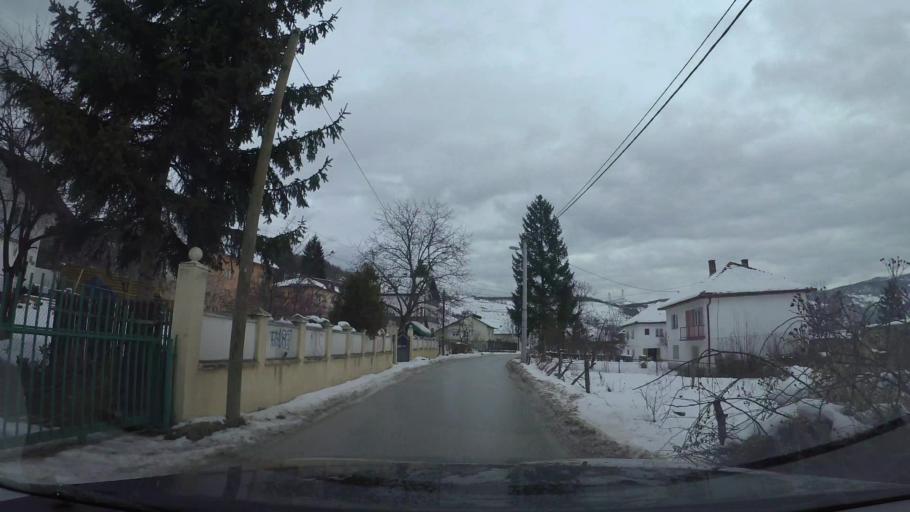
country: BA
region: Federation of Bosnia and Herzegovina
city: Vogosca
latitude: 43.8857
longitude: 18.3063
